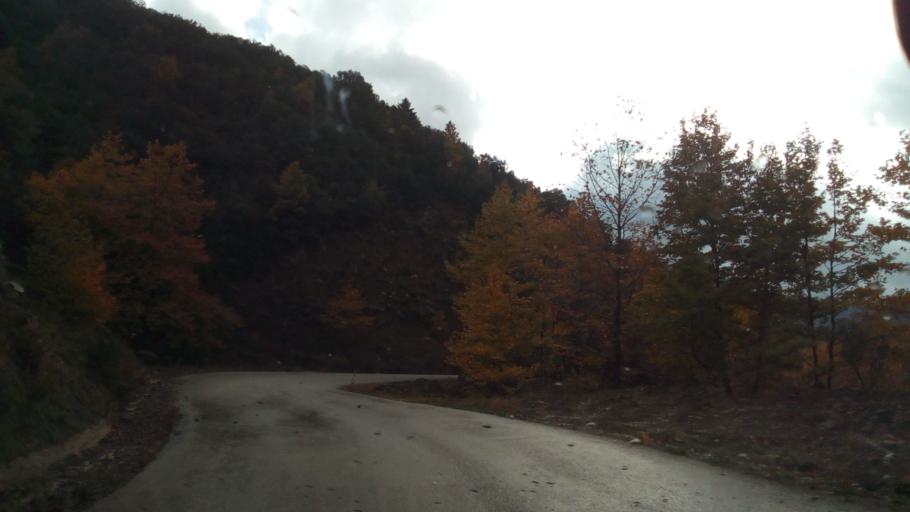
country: GR
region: West Greece
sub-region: Nomos Aitolias kai Akarnanias
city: Thermo
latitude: 38.6738
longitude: 21.8512
